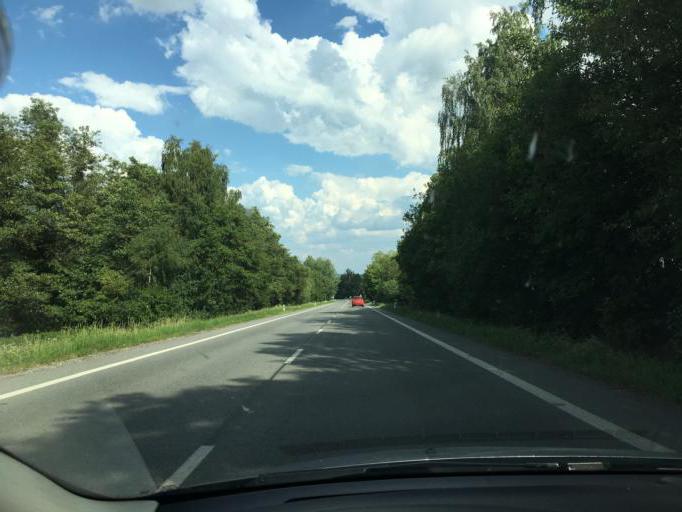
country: CZ
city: Horni Branna
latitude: 50.6200
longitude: 15.5821
